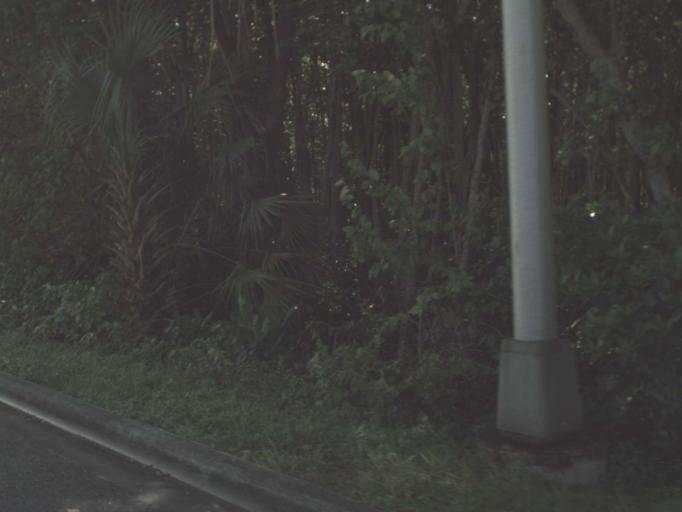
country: US
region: Florida
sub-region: Miami-Dade County
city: North Miami Beach
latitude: 25.9260
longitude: -80.1455
